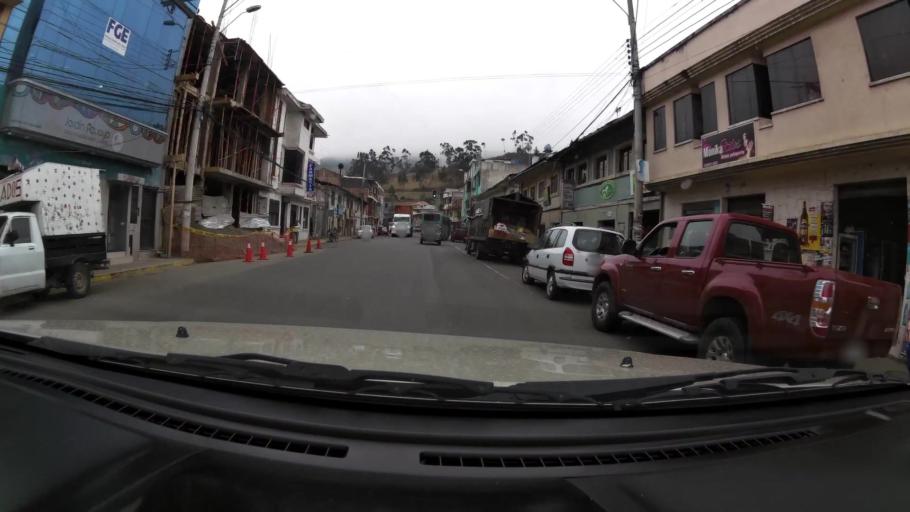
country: EC
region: Canar
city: Canar
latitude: -2.5090
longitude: -78.9264
